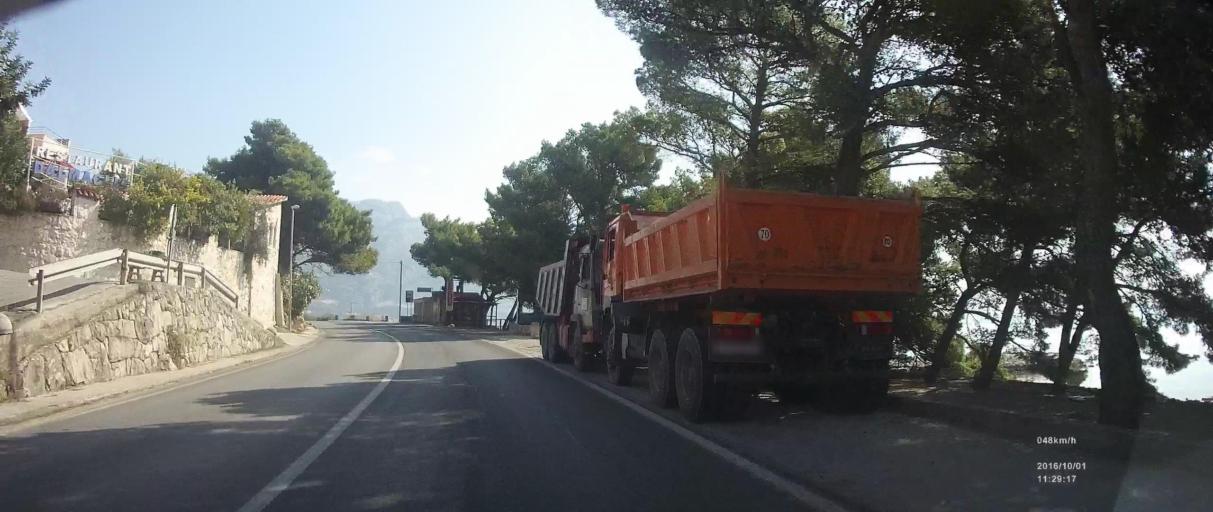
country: HR
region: Splitsko-Dalmatinska
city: Duce
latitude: 43.4394
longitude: 16.6647
